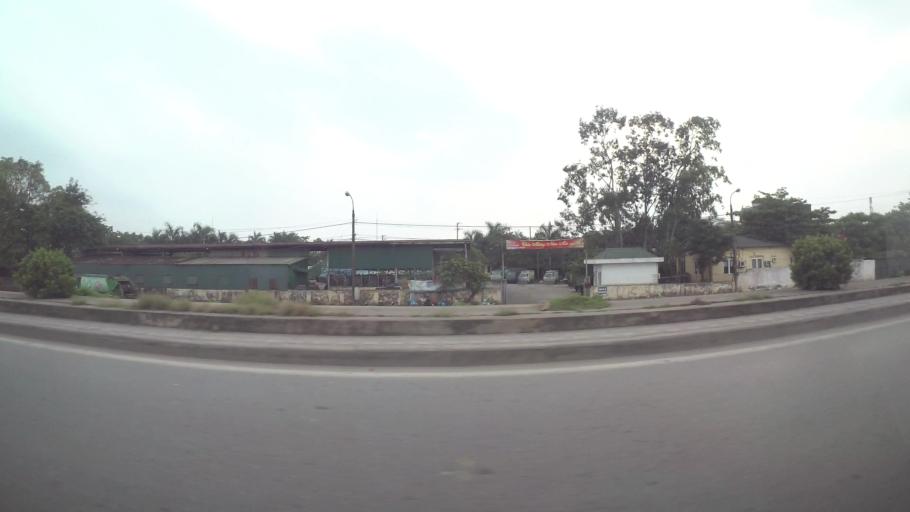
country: VN
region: Ha Noi
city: Hoan Kiem
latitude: 21.0366
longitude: 105.8707
